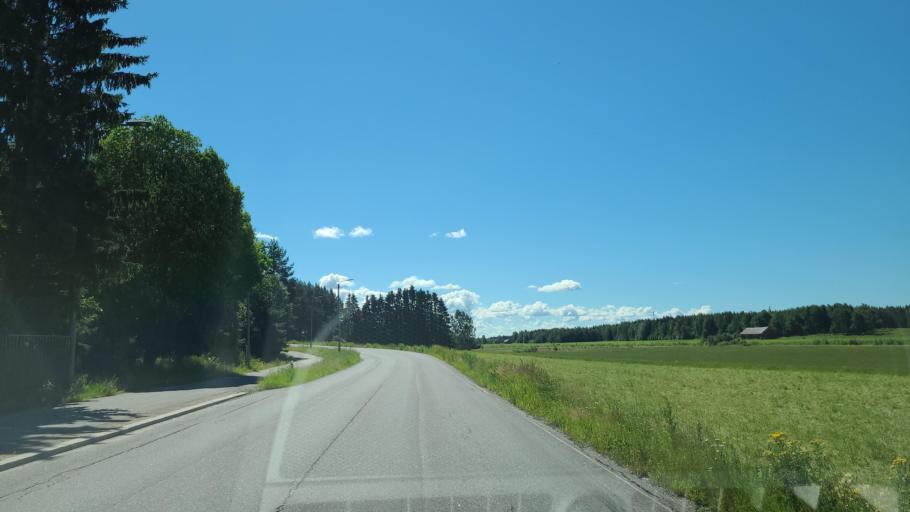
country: FI
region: Ostrobothnia
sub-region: Vaasa
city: Ristinummi
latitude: 63.0637
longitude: 21.7255
